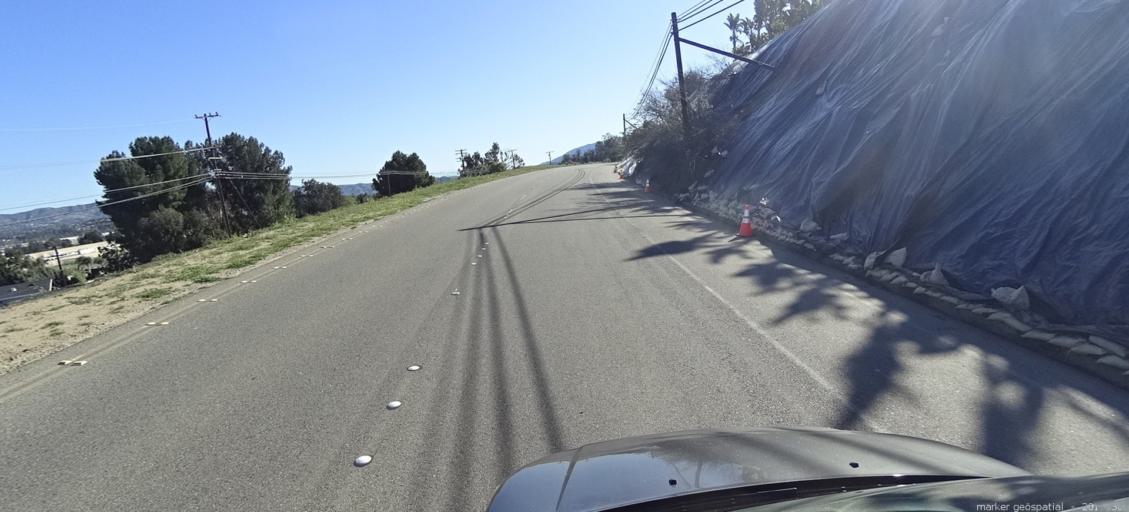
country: US
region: California
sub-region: Orange County
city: Villa Park
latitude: 33.8502
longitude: -117.8117
